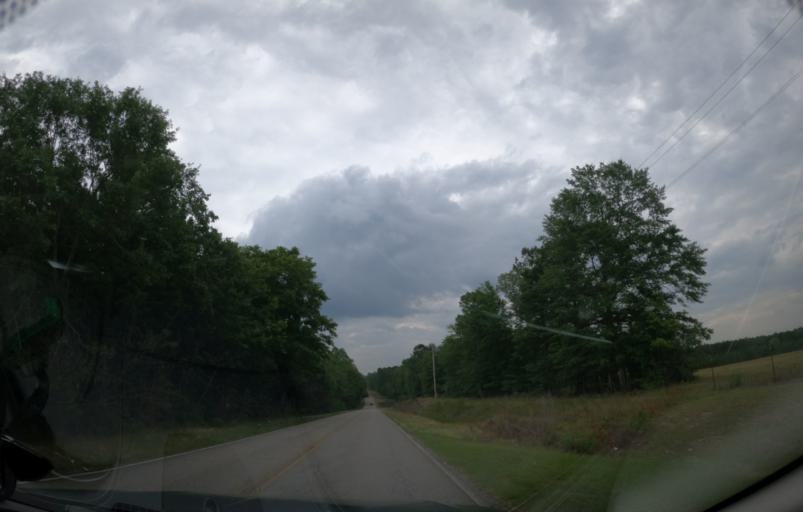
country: US
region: South Carolina
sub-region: Lexington County
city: Gaston
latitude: 33.6359
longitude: -81.2693
